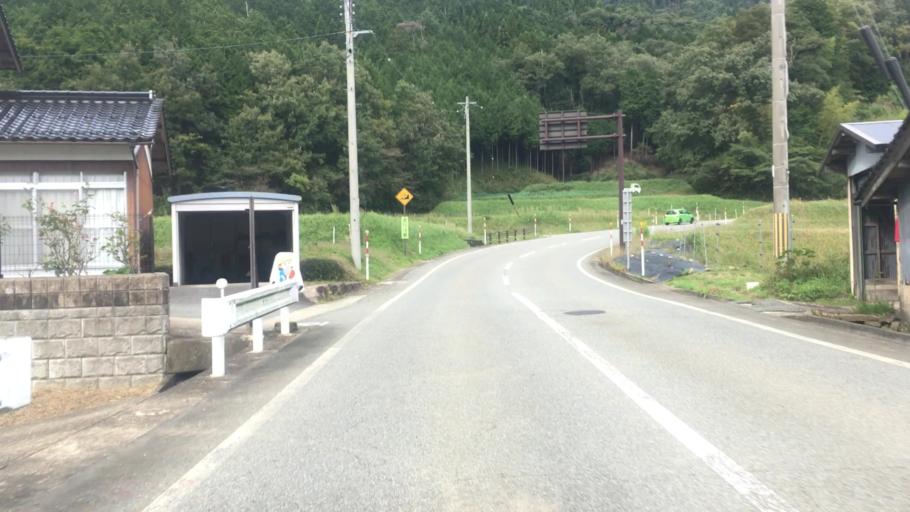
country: JP
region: Hyogo
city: Toyooka
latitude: 35.4121
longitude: 134.7342
